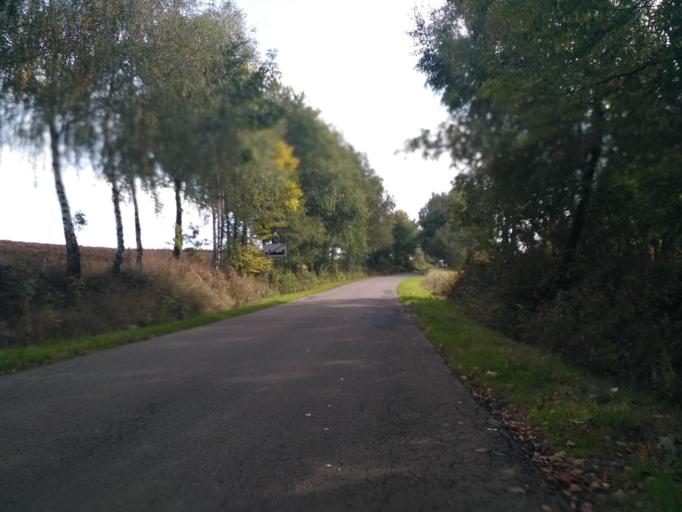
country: PL
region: Subcarpathian Voivodeship
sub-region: Powiat ropczycko-sedziszowski
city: Wielopole Skrzynskie
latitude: 49.9292
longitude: 21.5645
